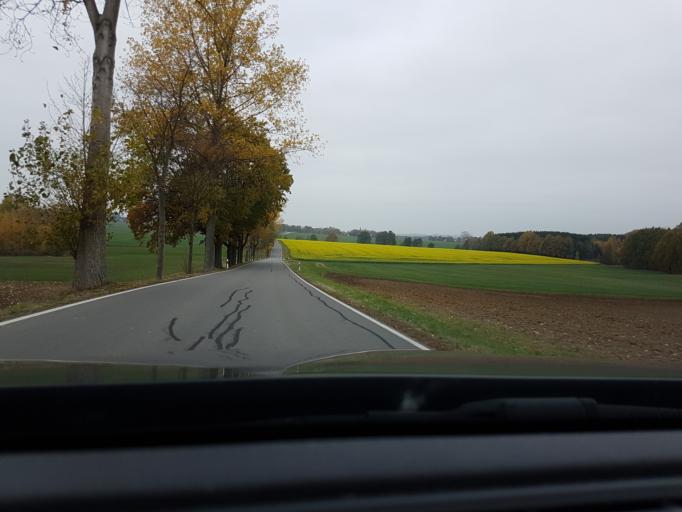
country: DE
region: Saxony
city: Altmittweida
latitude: 50.9737
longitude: 12.9437
